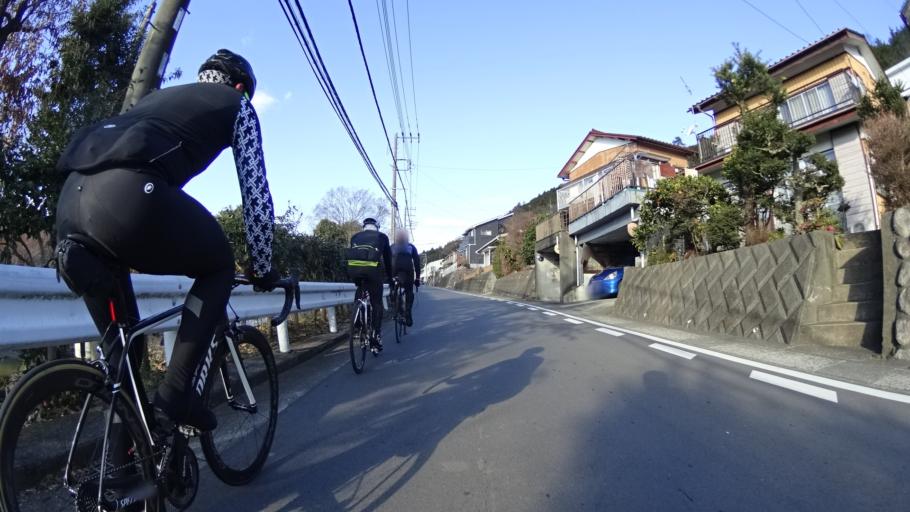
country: JP
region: Tokyo
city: Hachioji
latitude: 35.5678
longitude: 139.2585
